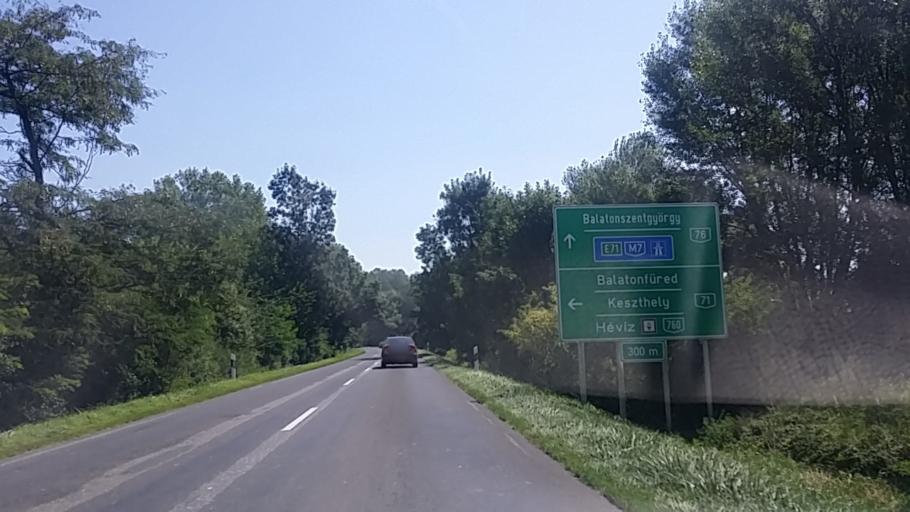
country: HU
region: Zala
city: Keszthely
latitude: 46.7028
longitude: 17.2485
